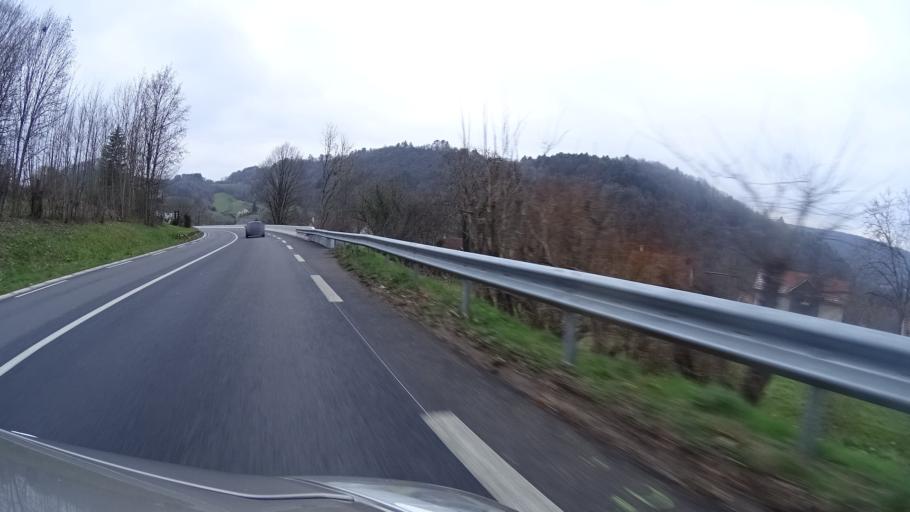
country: FR
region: Franche-Comte
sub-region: Departement du Doubs
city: Morre
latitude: 47.2227
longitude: 6.0668
